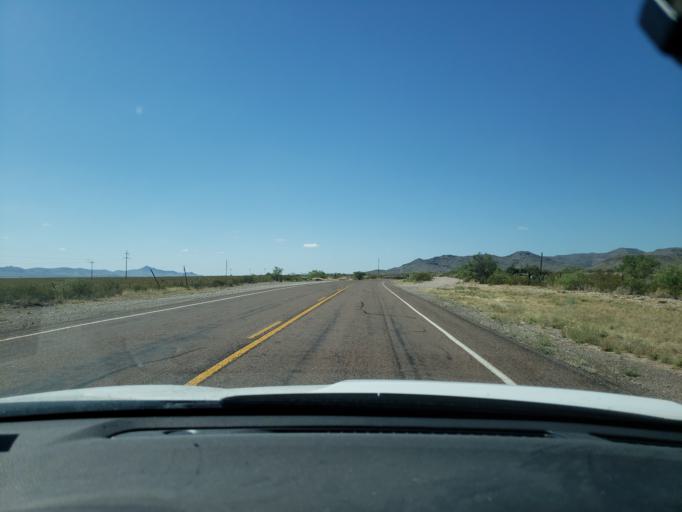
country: US
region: Texas
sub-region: Culberson County
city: Van Horn
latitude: 30.9338
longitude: -104.8097
